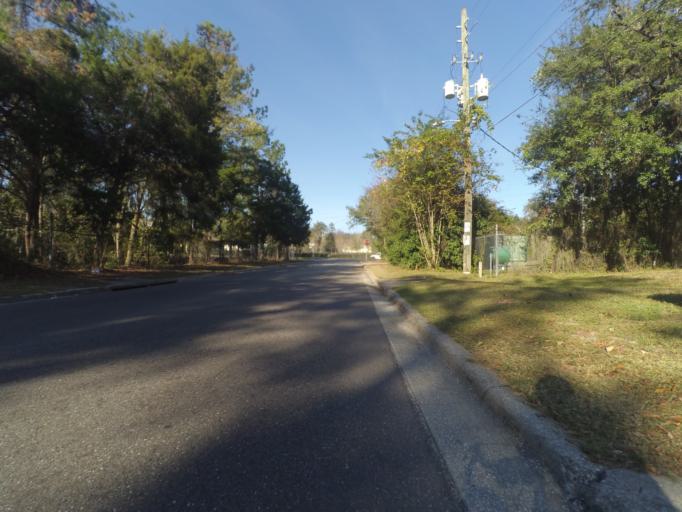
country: US
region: Florida
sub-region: Alachua County
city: Gainesville
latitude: 29.6192
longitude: -82.3656
